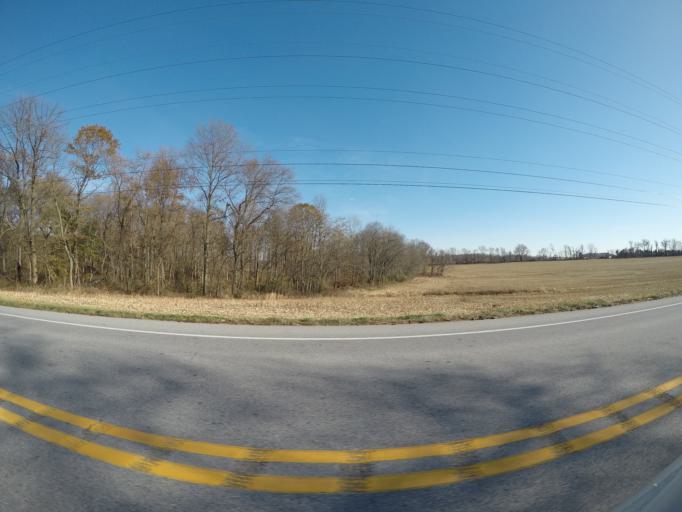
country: US
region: Pennsylvania
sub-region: Chester County
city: Parkesburg
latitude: 39.9283
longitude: -75.9151
